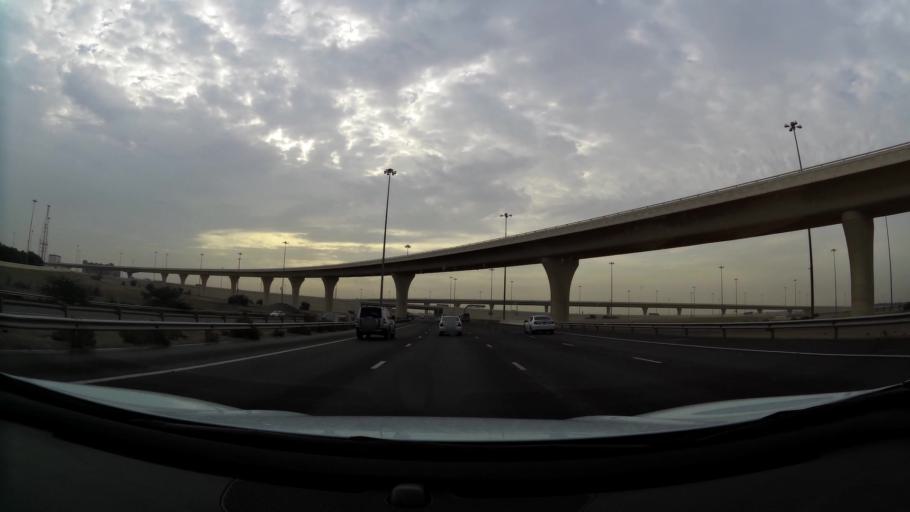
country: AE
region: Abu Dhabi
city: Abu Dhabi
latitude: 24.3111
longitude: 54.5979
